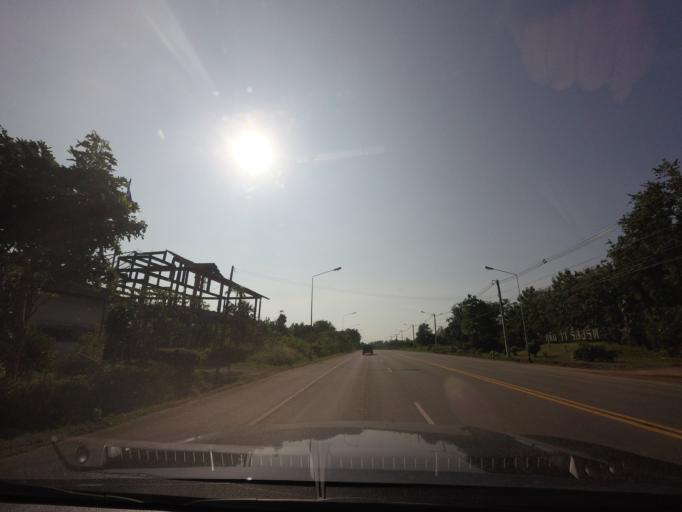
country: TH
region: Phetchabun
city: Lom Kao
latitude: 16.8403
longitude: 101.1797
